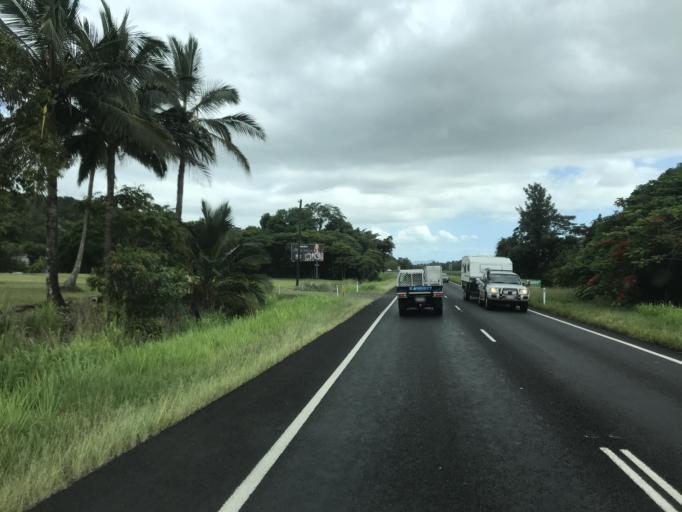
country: AU
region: Queensland
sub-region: Cassowary Coast
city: Innisfail
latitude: -17.6815
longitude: 146.0443
